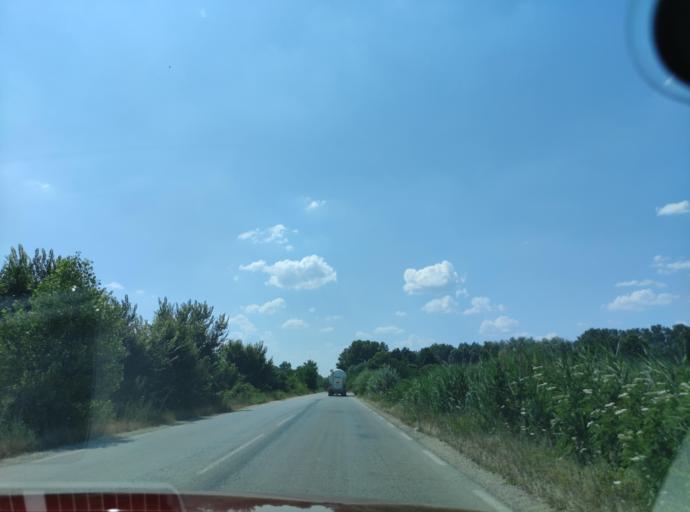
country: BG
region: Pleven
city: Iskur
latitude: 43.4535
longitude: 24.2436
